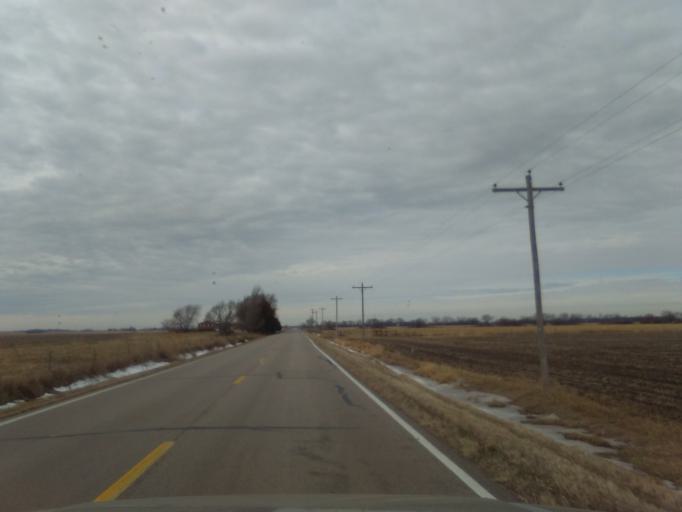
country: US
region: Nebraska
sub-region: Hall County
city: Grand Island
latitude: 40.7709
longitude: -98.4196
